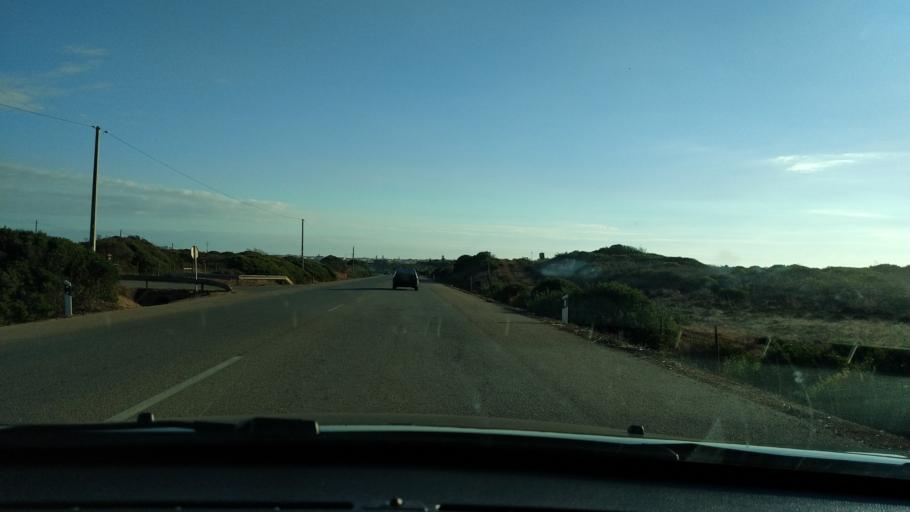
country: PT
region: Faro
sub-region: Vila do Bispo
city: Sagres
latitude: 37.0276
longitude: -8.9371
